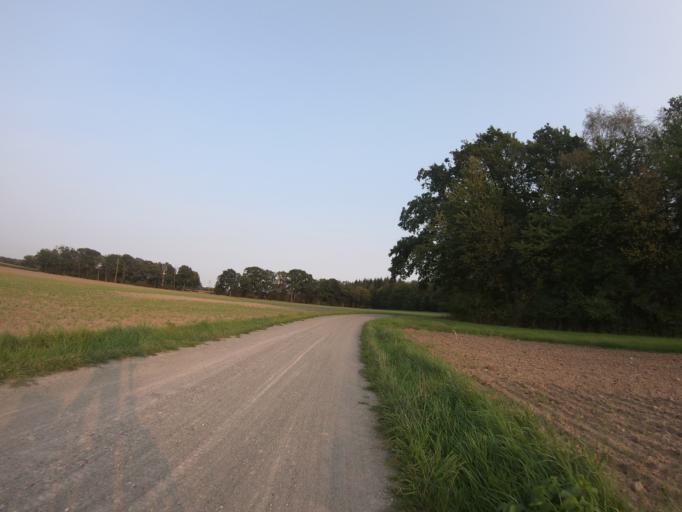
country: DE
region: Lower Saxony
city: Leiferde
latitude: 52.4293
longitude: 10.4663
